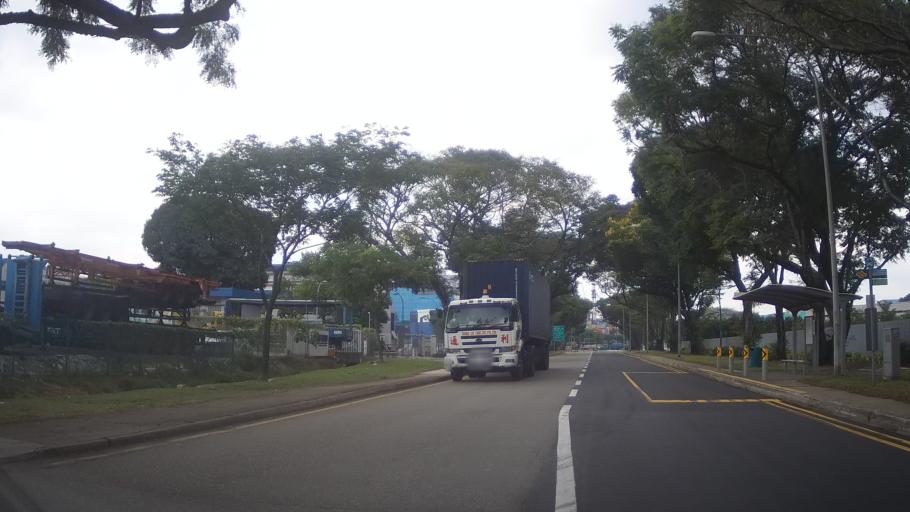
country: SG
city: Singapore
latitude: 1.3062
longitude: 103.6790
